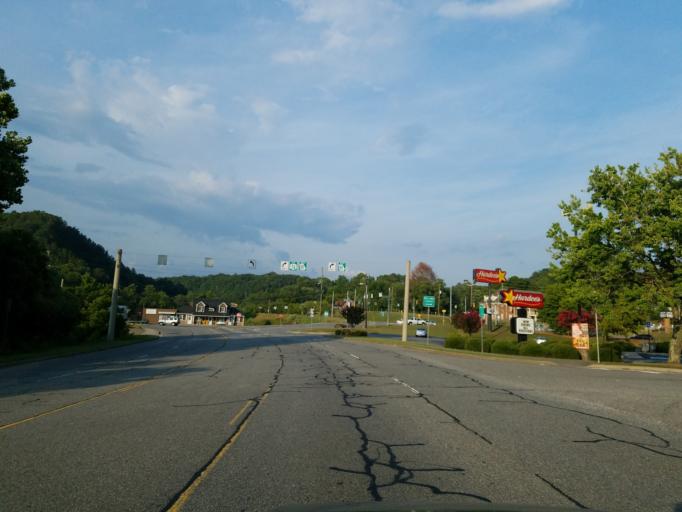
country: US
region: Georgia
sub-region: Gilmer County
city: Ellijay
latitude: 34.6850
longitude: -84.4750
